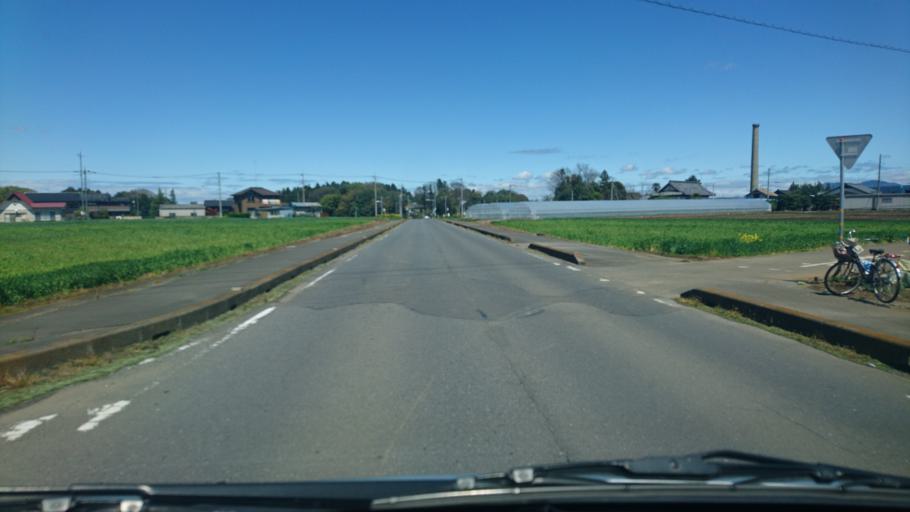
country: JP
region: Ibaraki
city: Shimodate
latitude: 36.2321
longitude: 139.9497
